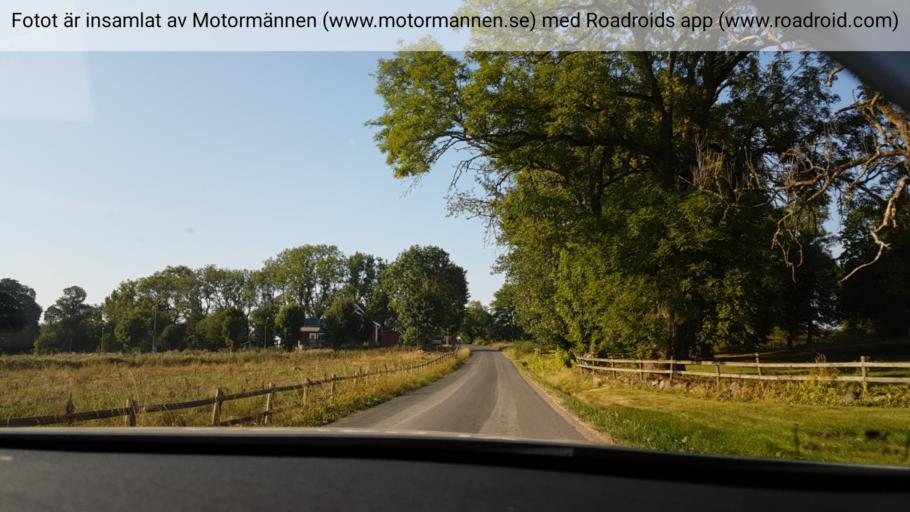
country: SE
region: Vaestra Goetaland
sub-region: Skovde Kommun
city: Stopen
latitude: 58.5053
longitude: 13.7800
